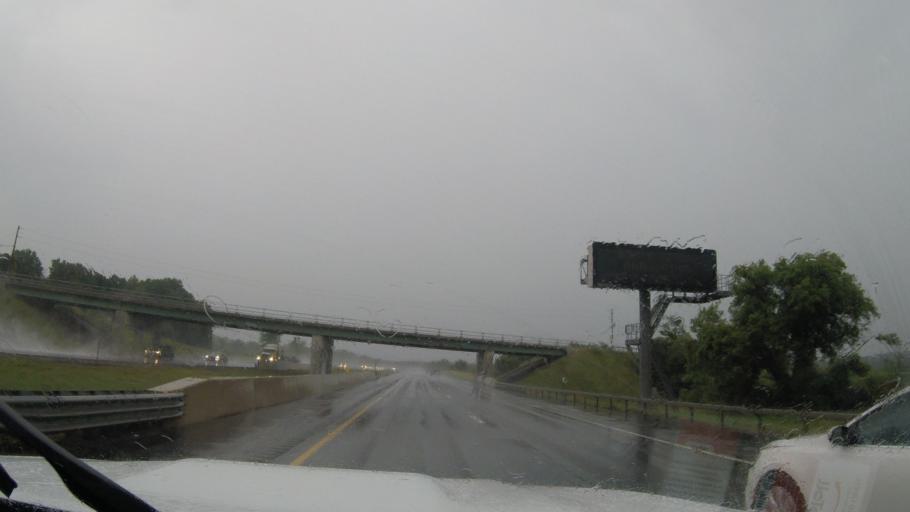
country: US
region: New York
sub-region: Ontario County
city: Phelps
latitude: 42.9625
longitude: -77.0432
